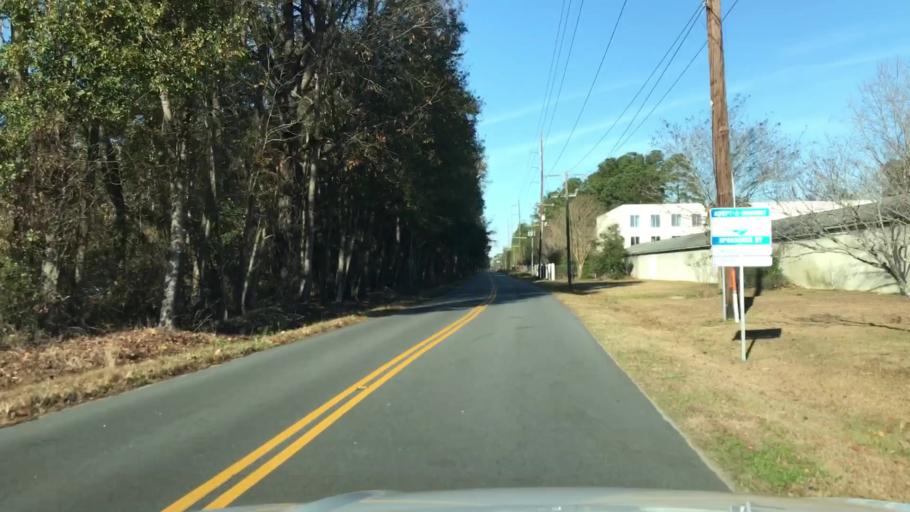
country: US
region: South Carolina
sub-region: Berkeley County
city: Ladson
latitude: 32.9861
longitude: -80.1106
